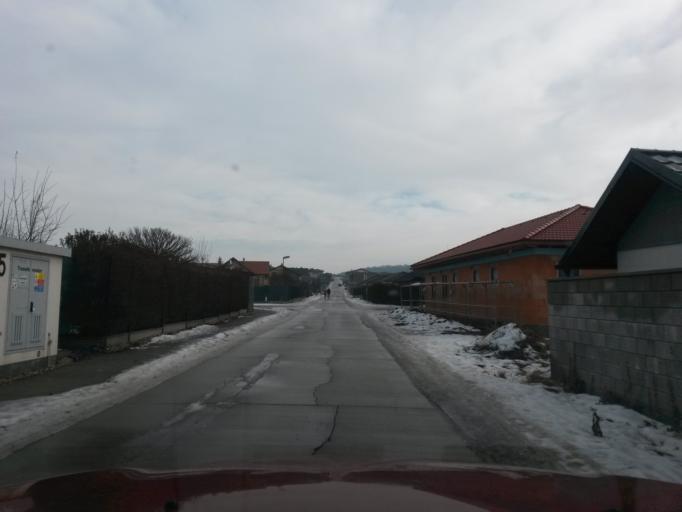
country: SK
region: Kosicky
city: Kosice
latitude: 48.7834
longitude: 21.3260
